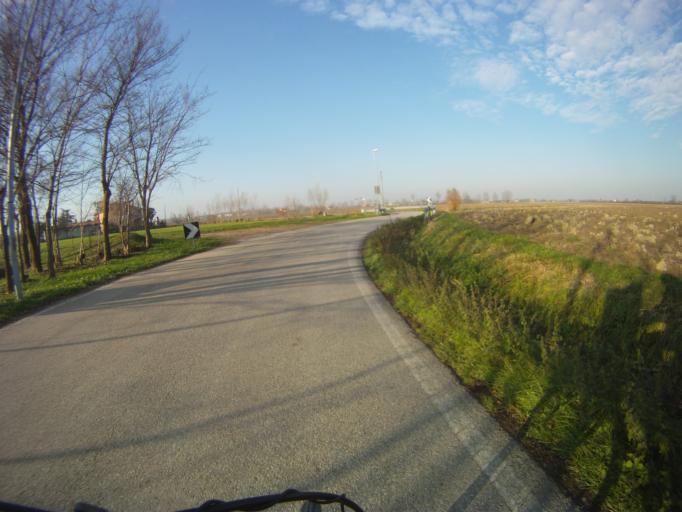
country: IT
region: Veneto
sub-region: Provincia di Padova
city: Polverara
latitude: 45.2897
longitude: 11.9641
